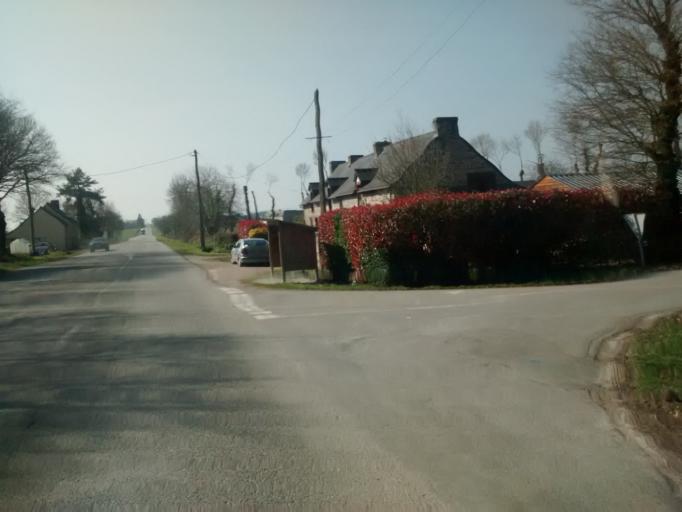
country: FR
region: Brittany
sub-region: Departement d'Ille-et-Vilaine
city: Maxent
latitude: 48.0196
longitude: -2.0484
